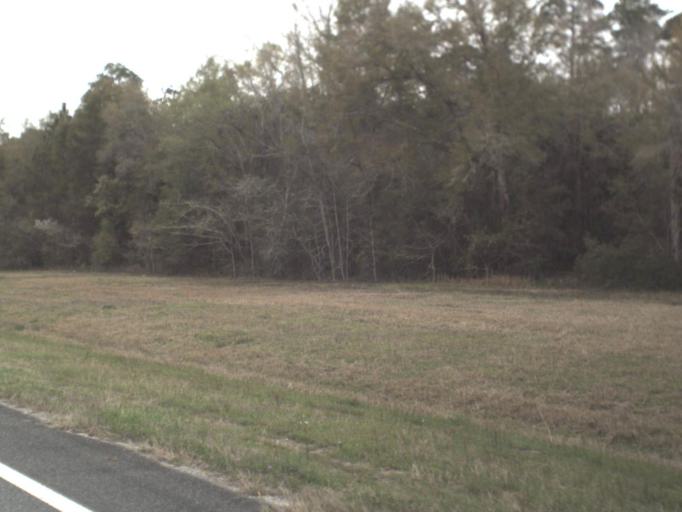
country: US
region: Florida
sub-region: Wakulla County
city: Crawfordville
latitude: 30.1528
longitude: -84.2701
